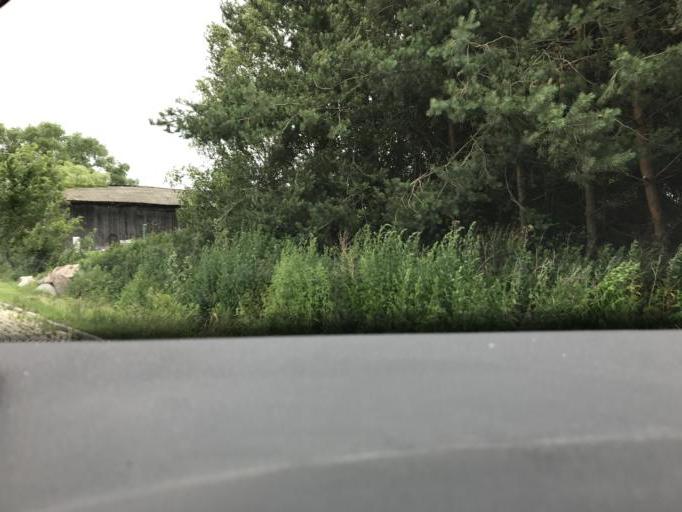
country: PL
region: Pomeranian Voivodeship
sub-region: Powiat gdanski
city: Pruszcz Gdanski
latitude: 54.2729
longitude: 18.6905
